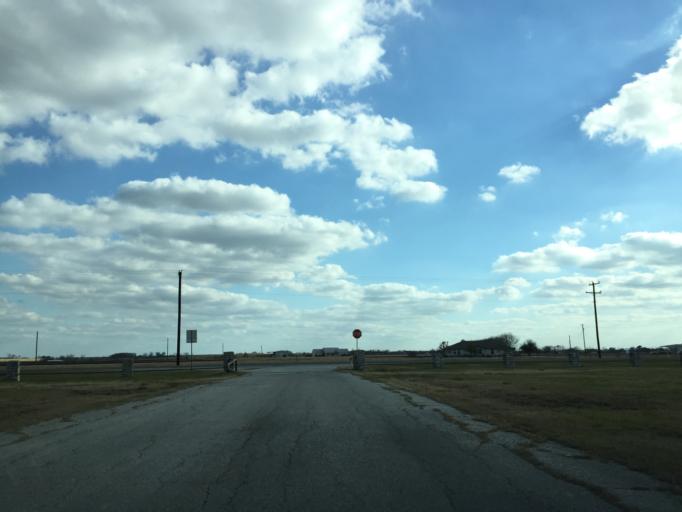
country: US
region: Texas
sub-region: Williamson County
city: Granger
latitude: 30.6646
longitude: -97.3647
